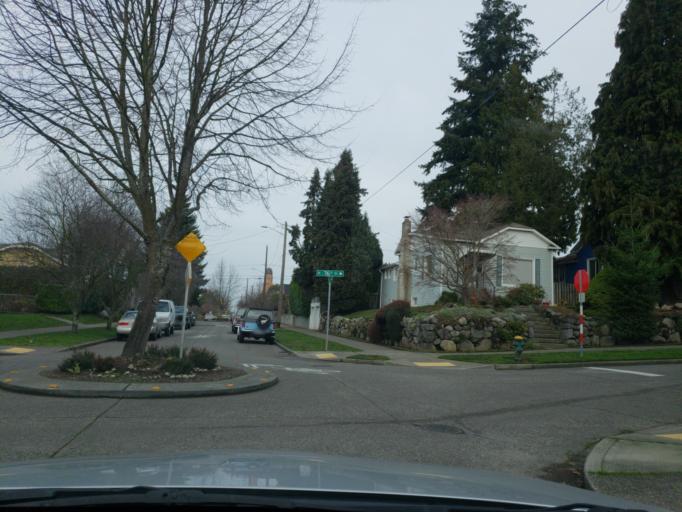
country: US
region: Washington
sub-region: King County
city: Shoreline
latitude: 47.6839
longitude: -122.3580
